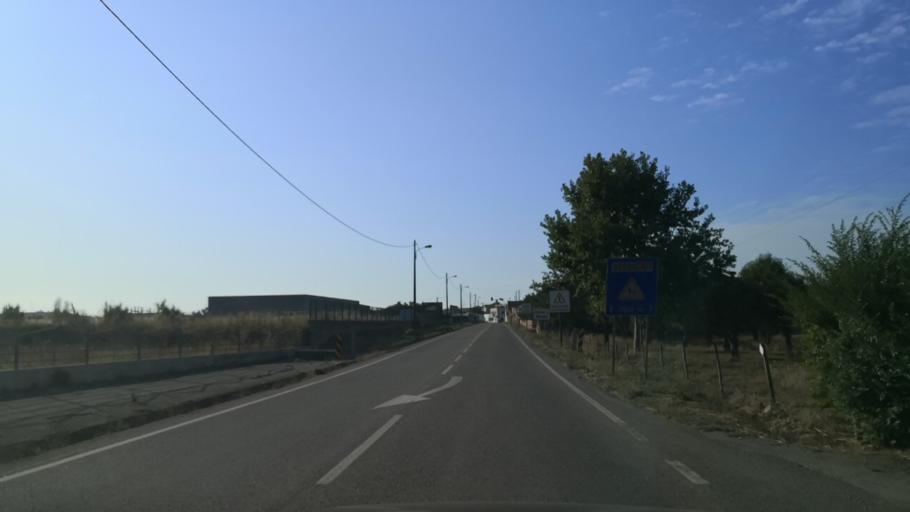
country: PT
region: Santarem
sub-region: Santarem
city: Santarem
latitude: 39.3339
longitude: -8.6604
